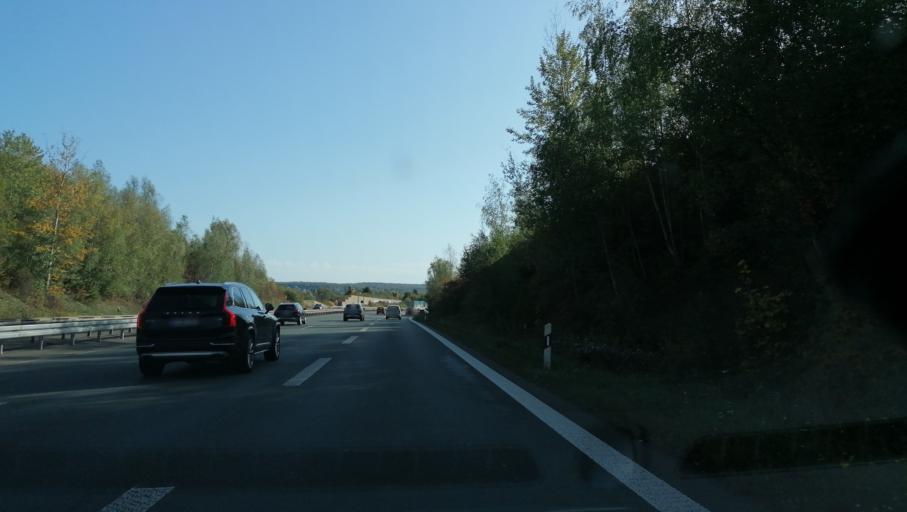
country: DE
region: North Rhine-Westphalia
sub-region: Regierungsbezirk Arnsberg
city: Dortmund
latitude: 51.4972
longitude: 7.5228
